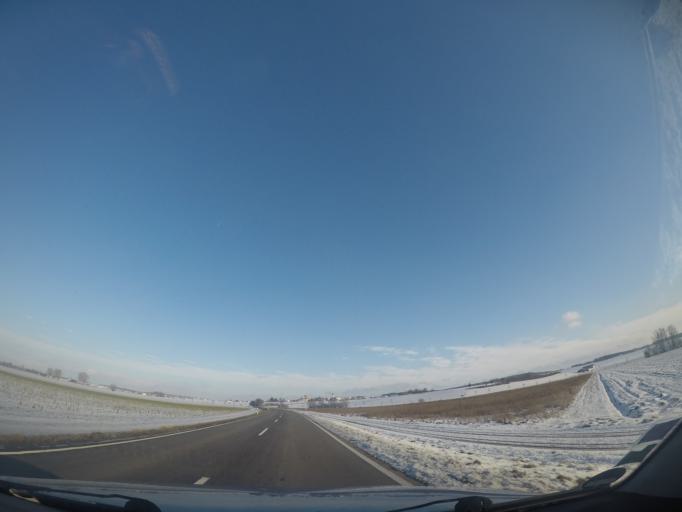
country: DE
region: Baden-Wuerttemberg
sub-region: Tuebingen Region
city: Dettingen
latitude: 48.2349
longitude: 9.7186
